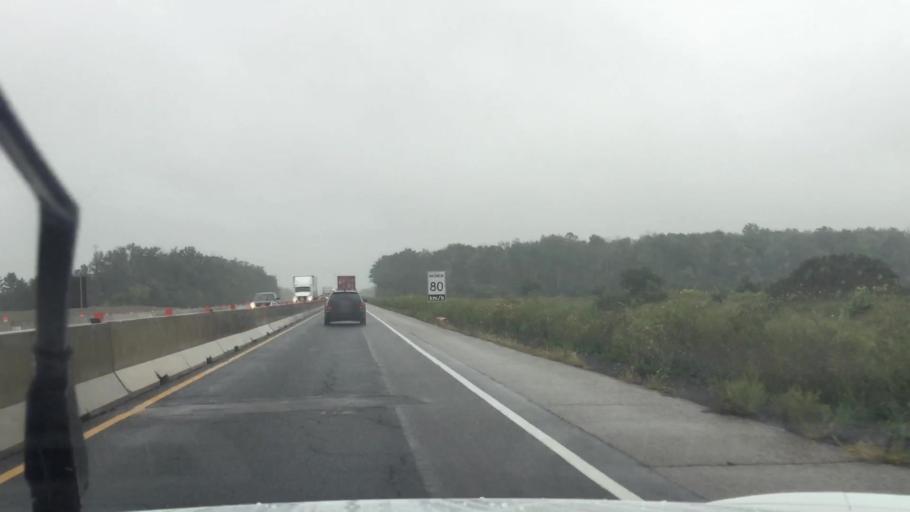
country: CA
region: Ontario
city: Delaware
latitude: 42.8112
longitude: -81.3231
